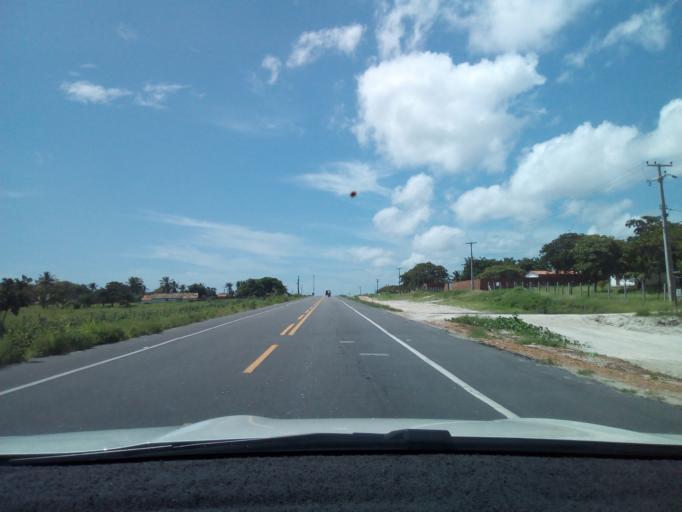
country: BR
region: Ceara
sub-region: Beberibe
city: Beberibe
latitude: -4.2636
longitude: -38.0638
